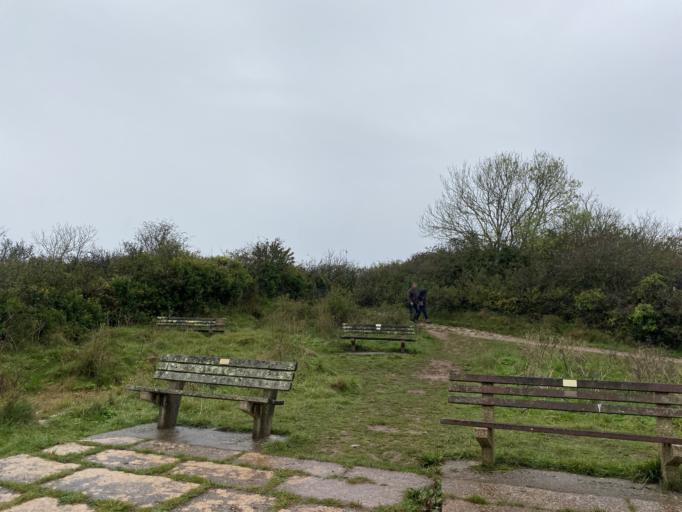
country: GB
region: England
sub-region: Borough of Torbay
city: Brixham
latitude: 50.4004
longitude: -3.4921
